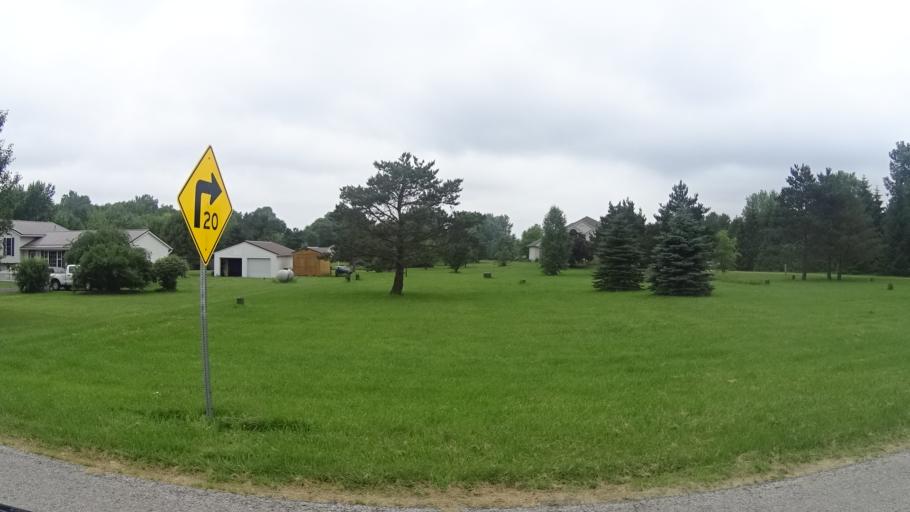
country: US
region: Ohio
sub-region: Erie County
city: Milan
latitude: 41.2858
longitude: -82.5499
